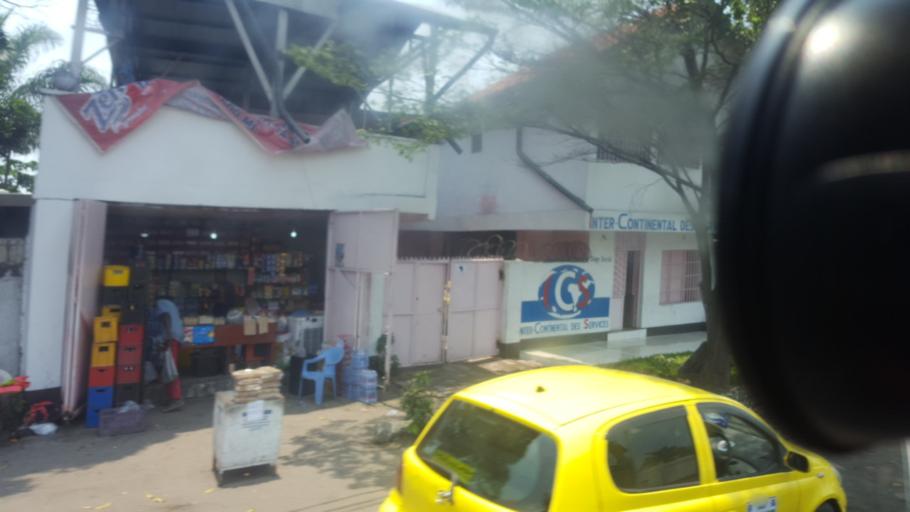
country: CD
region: Kinshasa
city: Masina
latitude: -4.3852
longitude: 15.3553
